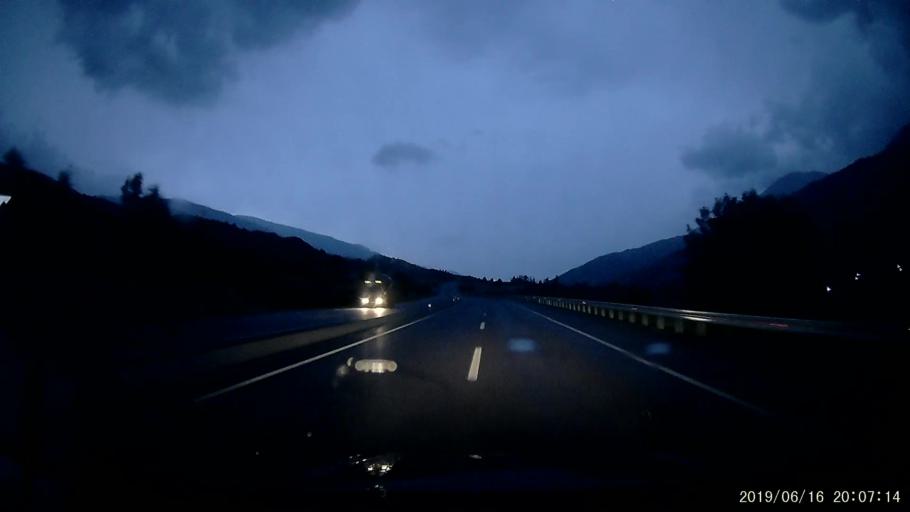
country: TR
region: Sivas
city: Dogansar
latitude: 40.3179
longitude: 37.6285
